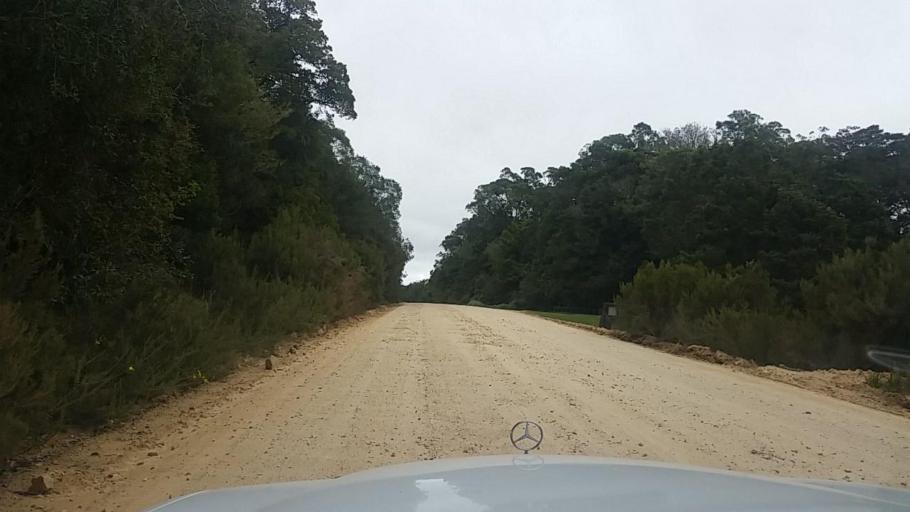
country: ZA
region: Western Cape
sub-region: Eden District Municipality
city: Knysna
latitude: -33.9624
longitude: 23.1576
